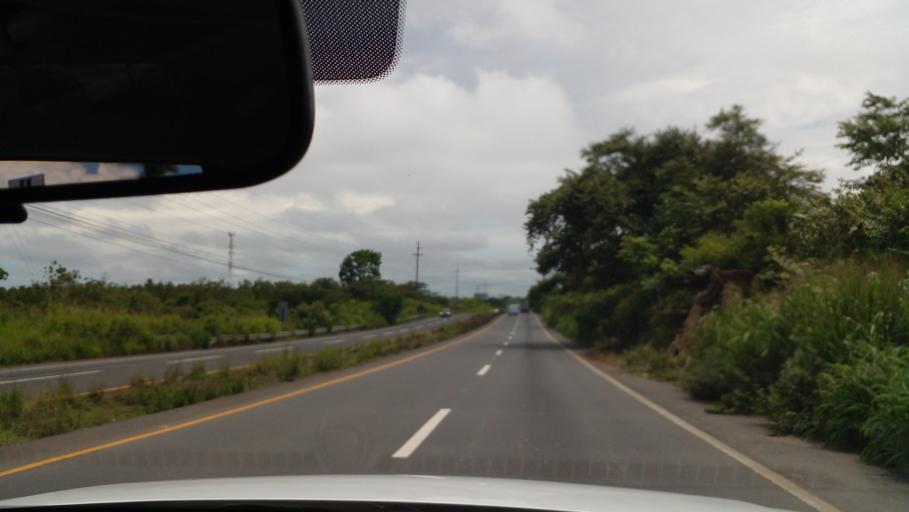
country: PA
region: Panama
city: Nueva Gorgona
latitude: 8.4662
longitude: -79.9675
